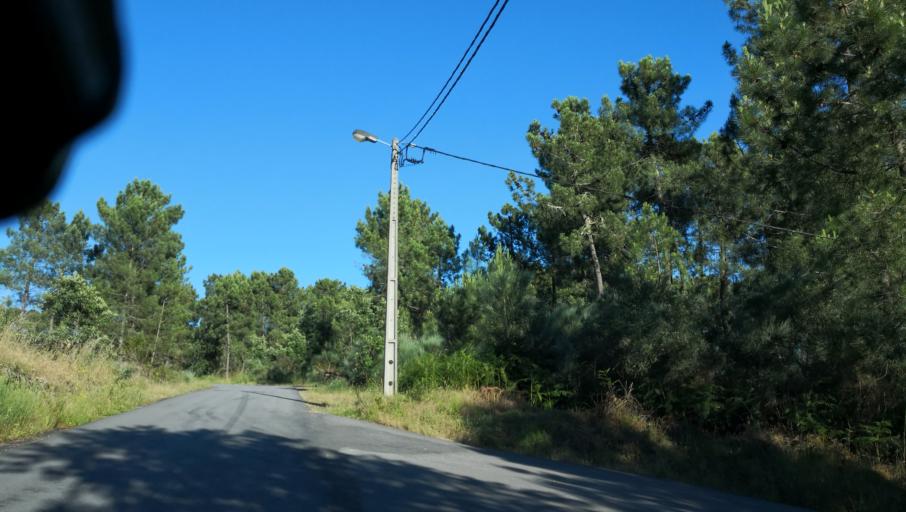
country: PT
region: Vila Real
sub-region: Vila Real
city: Vila Real
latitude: 41.3155
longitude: -7.6992
